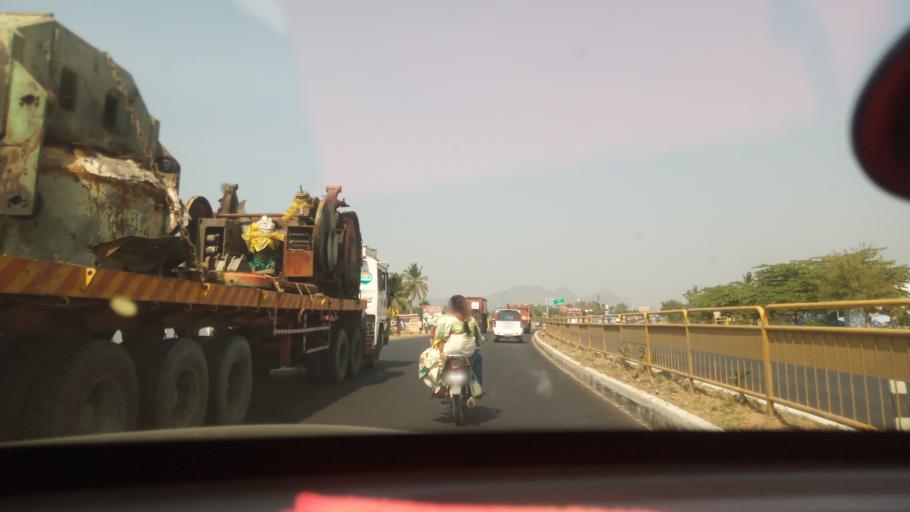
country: IN
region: Tamil Nadu
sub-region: Salem
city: Omalur
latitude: 11.8494
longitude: 78.0689
